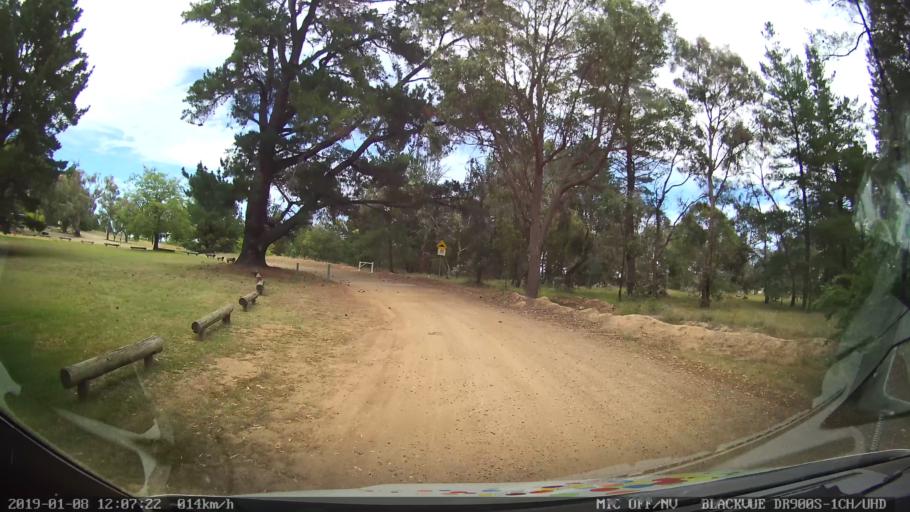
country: AU
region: New South Wales
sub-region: Armidale Dumaresq
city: Armidale
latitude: -30.4269
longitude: 151.5939
